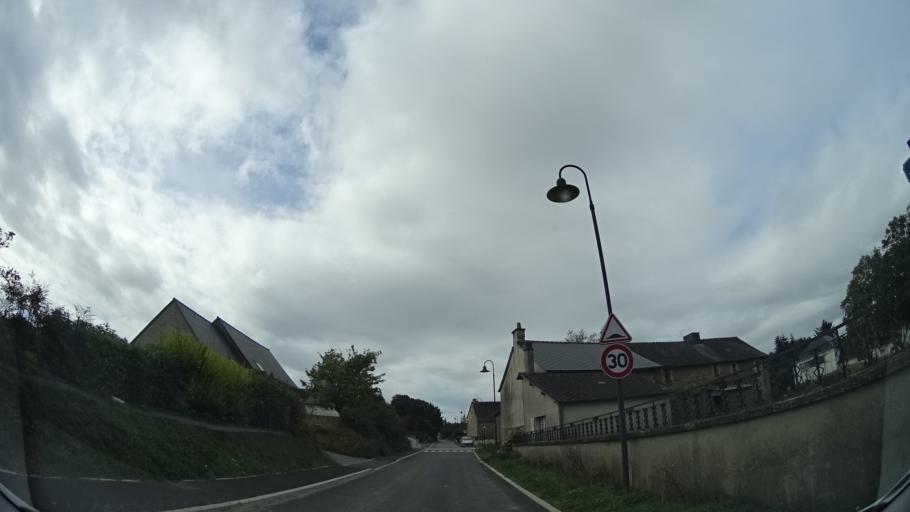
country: FR
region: Brittany
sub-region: Departement d'Ille-et-Vilaine
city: Tinteniac
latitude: 48.2885
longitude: -1.8874
